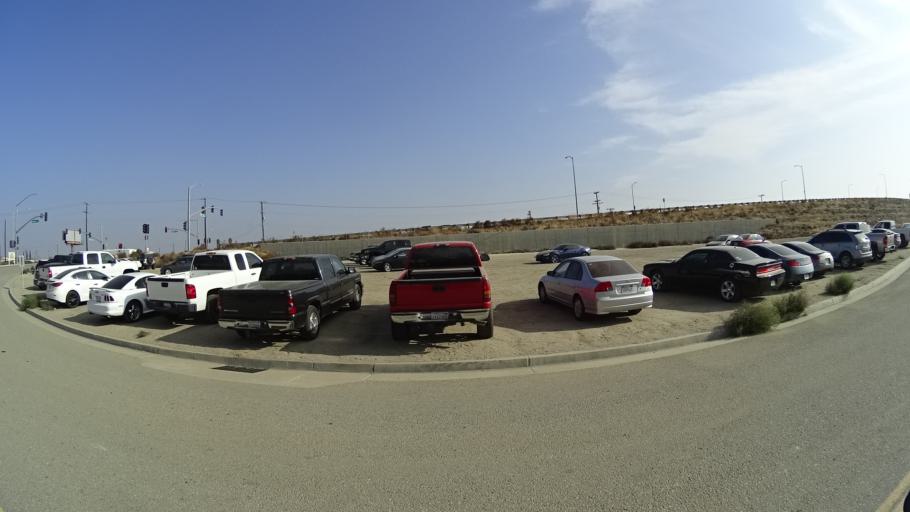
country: US
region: California
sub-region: Kern County
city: Greenacres
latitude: 35.3785
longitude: -119.0666
